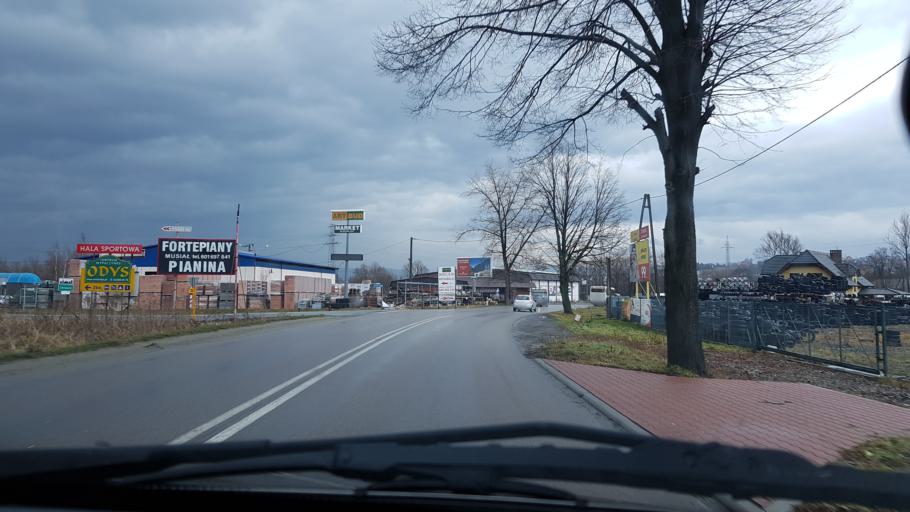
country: PL
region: Silesian Voivodeship
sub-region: Powiat zywiecki
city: Zarzecze
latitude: 49.7133
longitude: 19.1630
